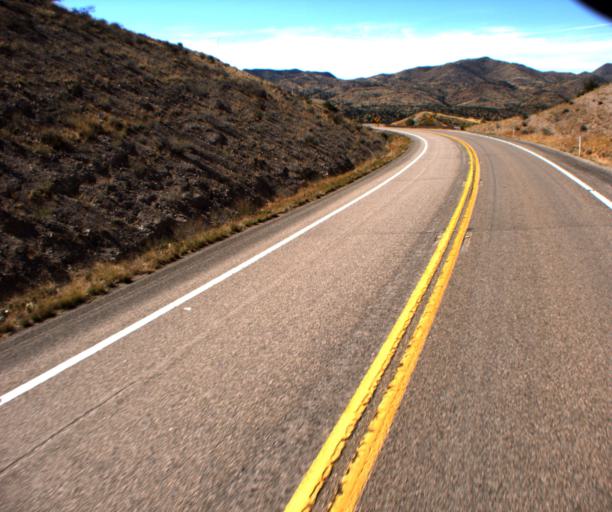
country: US
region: Arizona
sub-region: Pima County
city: Corona de Tucson
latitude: 31.8209
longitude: -110.7116
